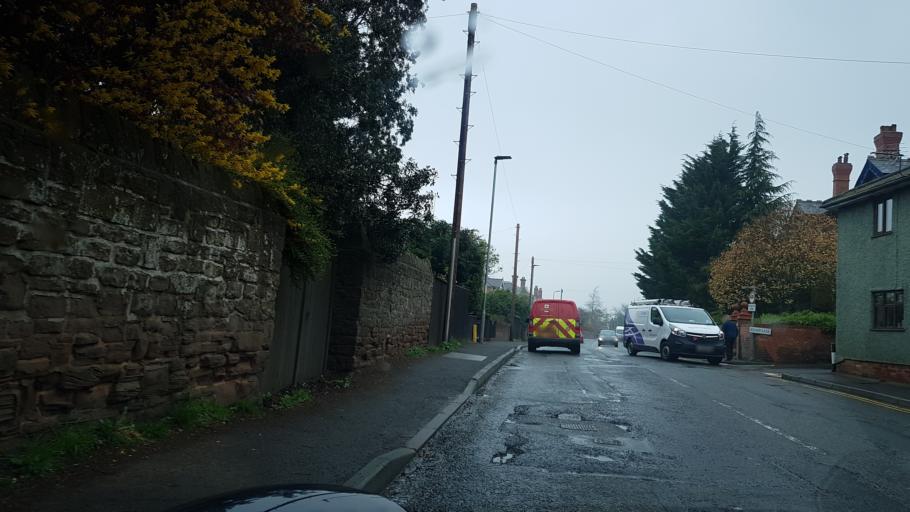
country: GB
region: England
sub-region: Herefordshire
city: Ledbury
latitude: 52.0421
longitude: -2.4256
